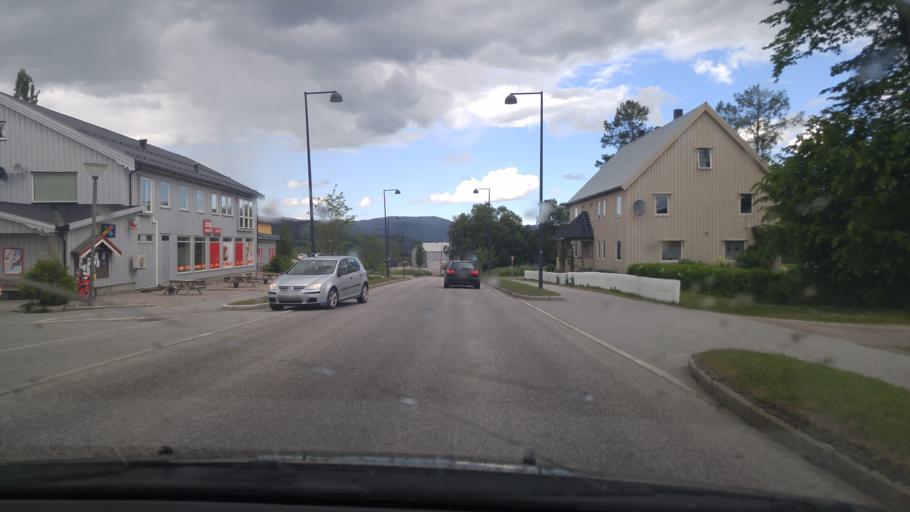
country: NO
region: Nord-Trondelag
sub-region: Namdalseid
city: Namdalseid
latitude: 64.2231
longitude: 11.2233
